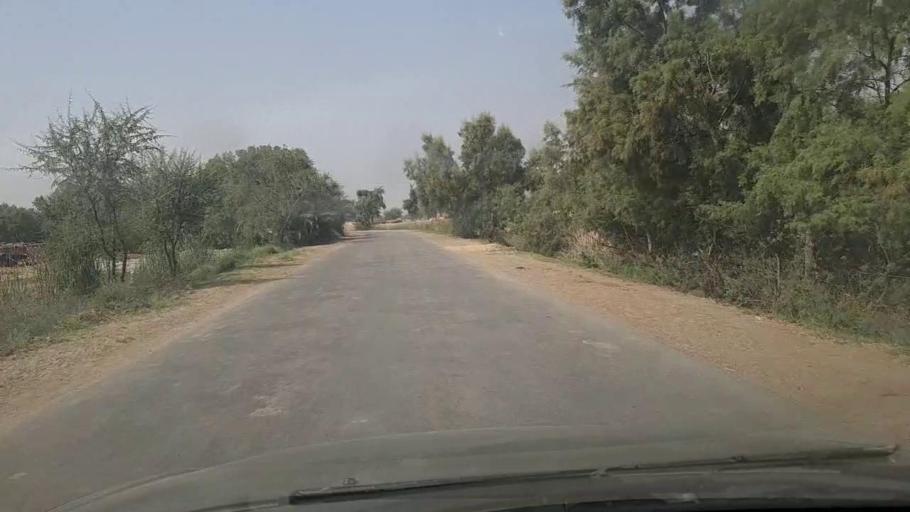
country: PK
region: Sindh
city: Khanpur
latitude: 27.8925
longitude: 69.4851
